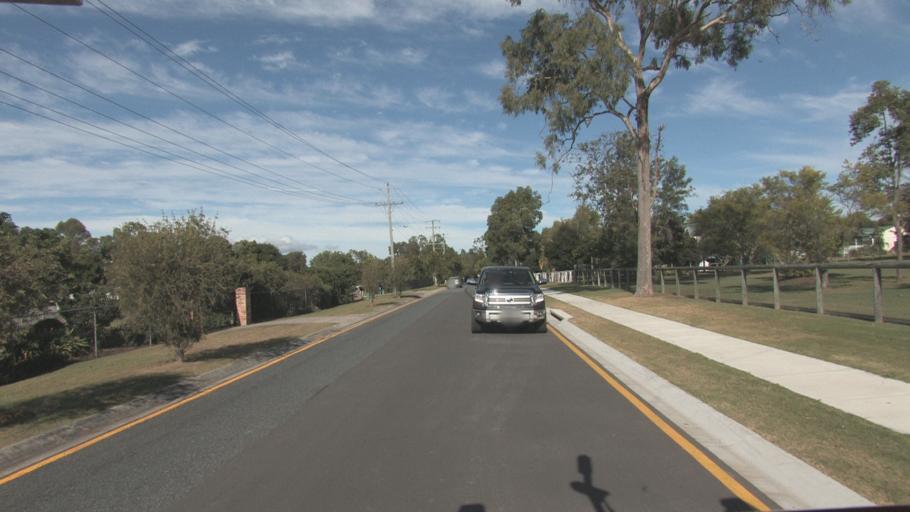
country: AU
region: Queensland
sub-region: Brisbane
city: Forest Lake
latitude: -27.6570
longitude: 152.9949
